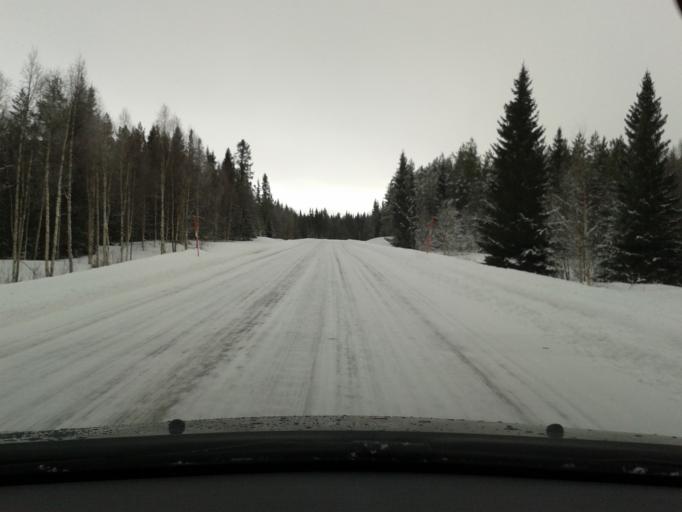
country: SE
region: Vaesterbotten
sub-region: Vilhelmina Kommun
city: Sjoberg
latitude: 64.8293
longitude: 15.9474
